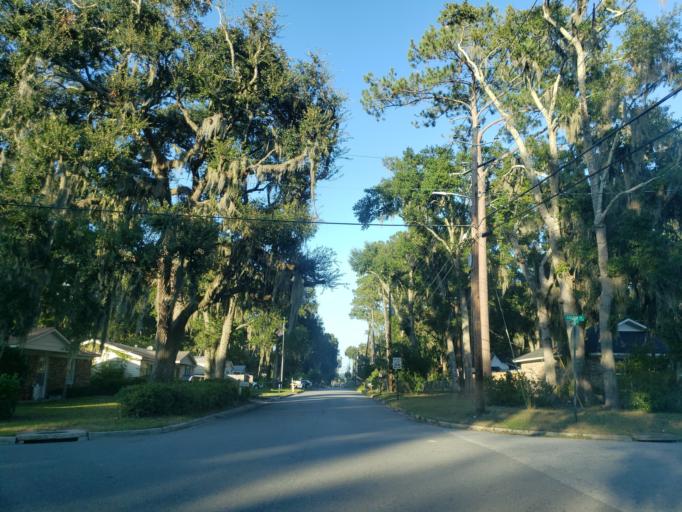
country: US
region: Georgia
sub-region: Chatham County
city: Isle of Hope
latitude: 31.9971
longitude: -81.0663
